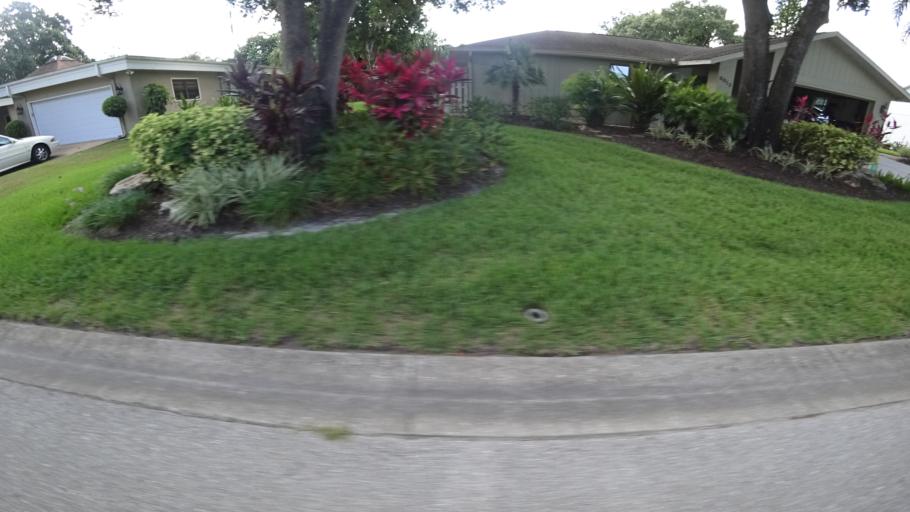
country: US
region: Florida
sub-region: Sarasota County
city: Desoto Lakes
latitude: 27.3972
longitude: -82.4946
